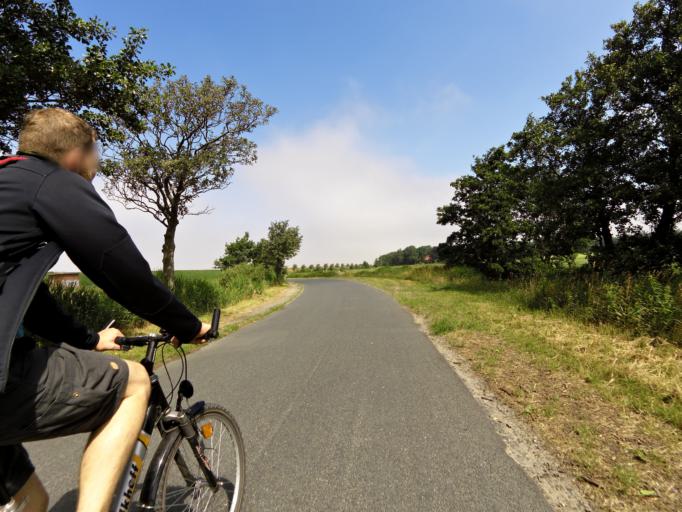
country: DE
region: Lower Saxony
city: Nordholz
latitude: 53.8305
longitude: 8.5815
